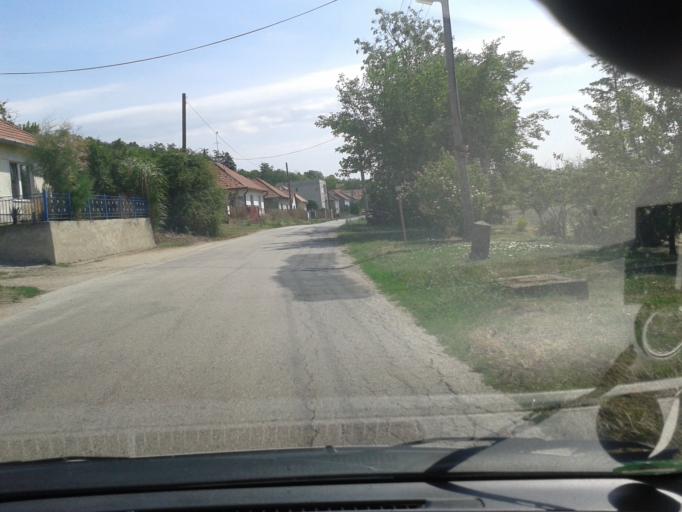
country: HU
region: Pest
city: Szob
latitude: 47.8280
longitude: 18.8106
